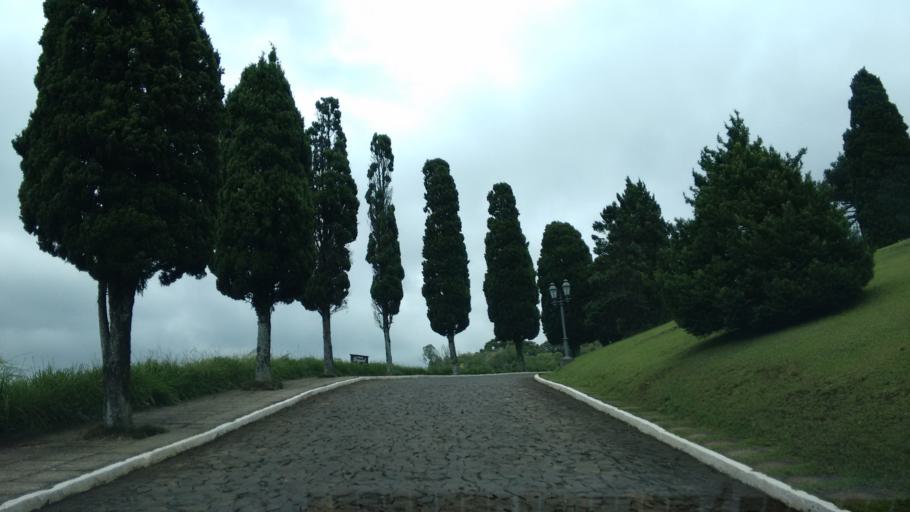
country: BR
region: Santa Catarina
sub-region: Videira
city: Videira
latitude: -27.0268
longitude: -50.9273
